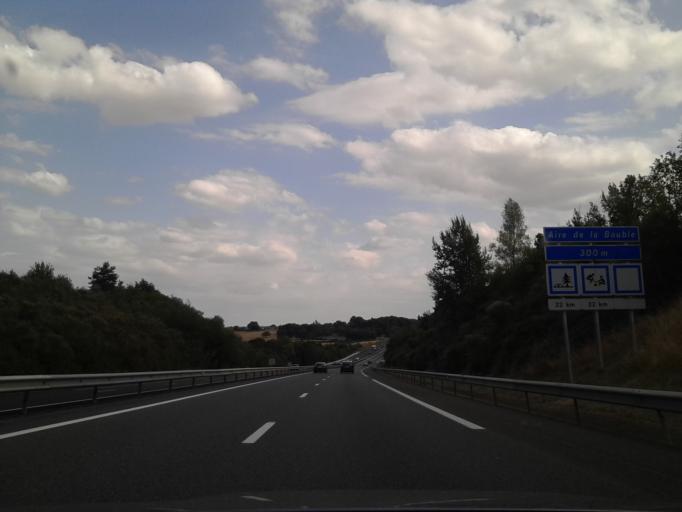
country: FR
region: Auvergne
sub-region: Departement de l'Allier
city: Bellenaves
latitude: 46.2379
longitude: 3.0963
